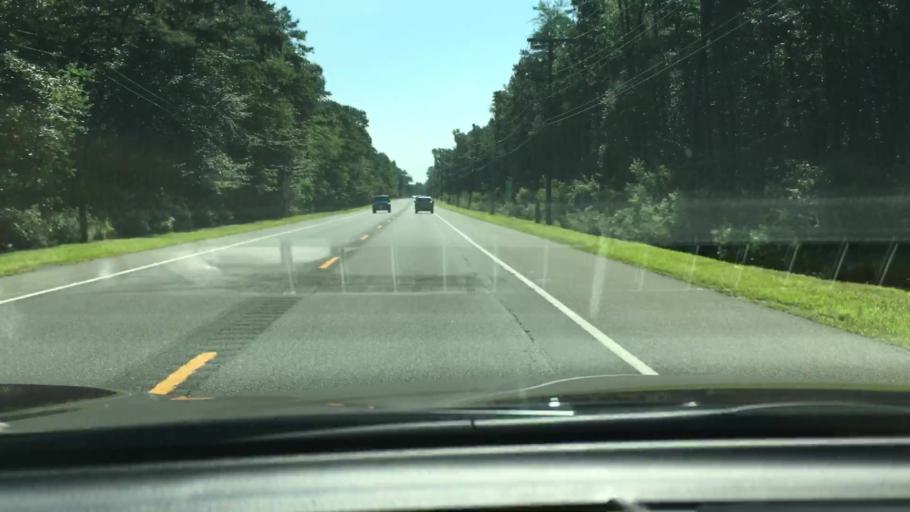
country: US
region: New Jersey
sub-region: Cumberland County
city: Laurel Lake
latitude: 39.3768
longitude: -74.9562
